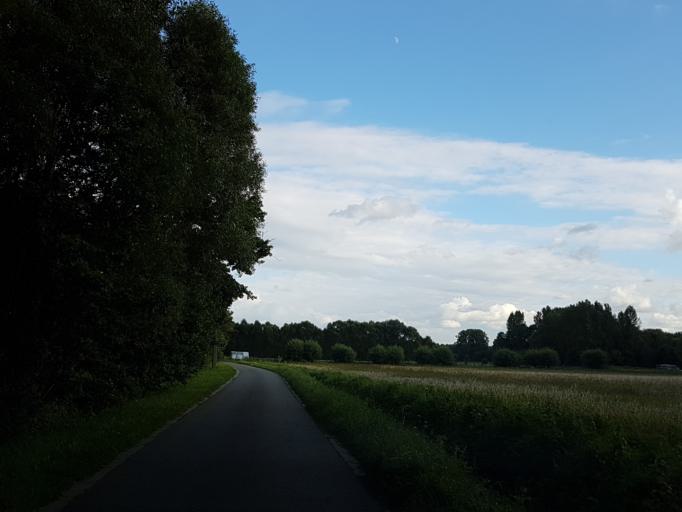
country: BE
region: Flanders
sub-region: Provincie Vlaams-Brabant
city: Kampenhout
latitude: 50.9281
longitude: 4.5956
